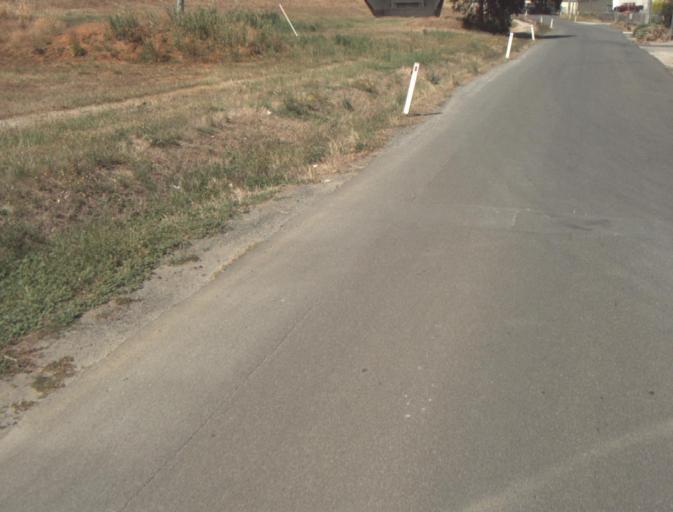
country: AU
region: Tasmania
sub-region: Launceston
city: East Launceston
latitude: -41.4192
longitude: 147.1428
